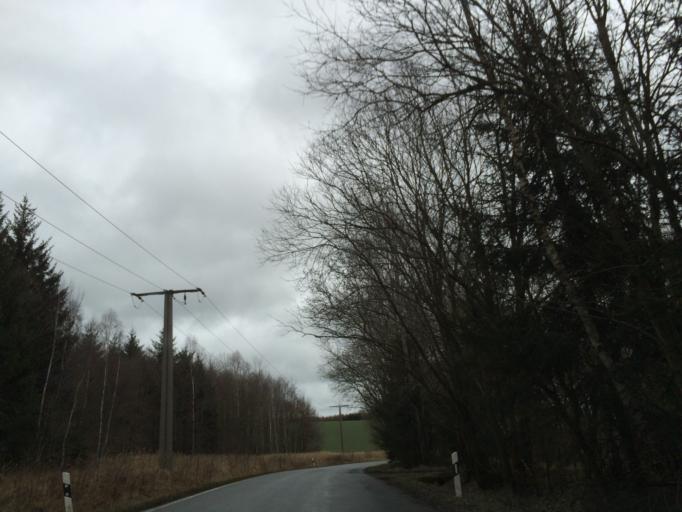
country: DE
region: Thuringia
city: Dreba
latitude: 50.6788
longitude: 11.7341
